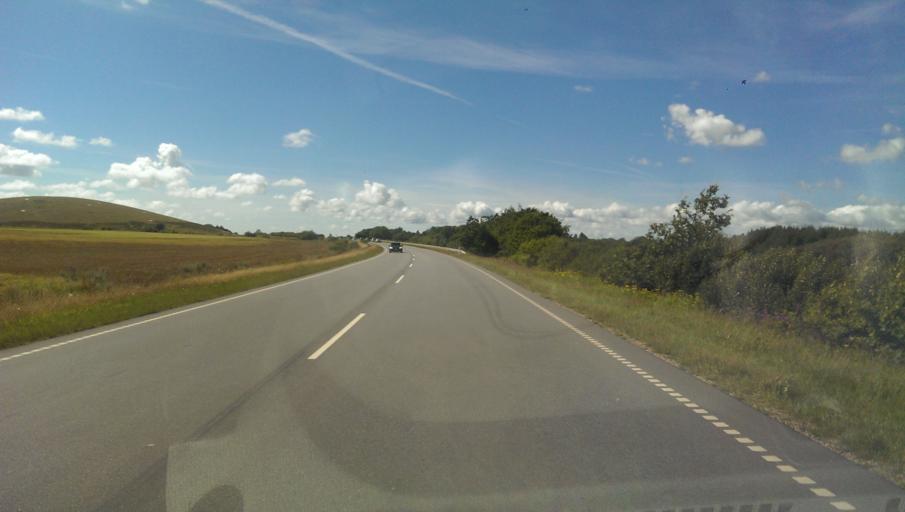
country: DK
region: South Denmark
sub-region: Esbjerg Kommune
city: Esbjerg
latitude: 55.5154
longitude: 8.4932
